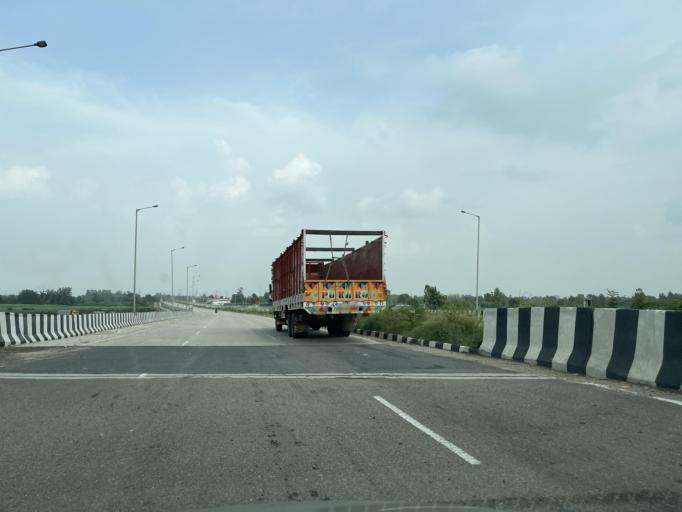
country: IN
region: Uttarakhand
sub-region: Udham Singh Nagar
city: Bazpur
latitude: 29.1492
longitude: 79.0594
